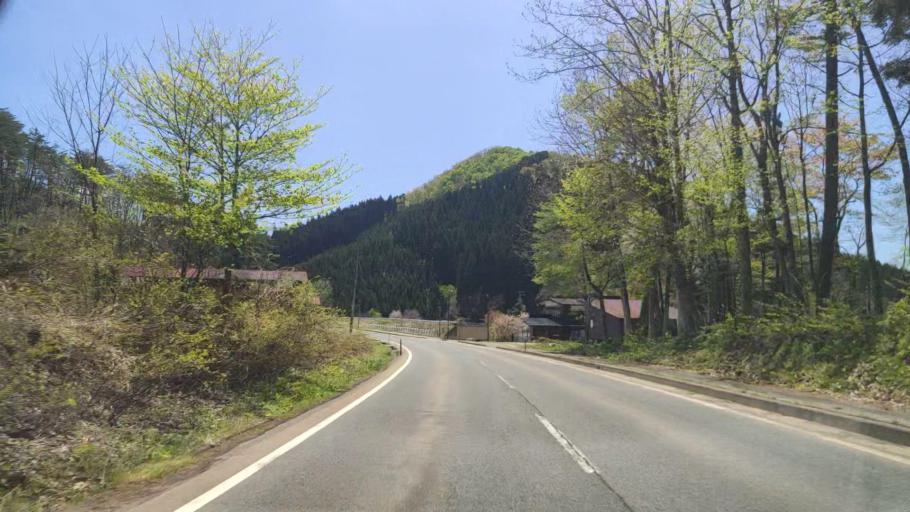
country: JP
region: Yamagata
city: Shinjo
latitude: 38.9102
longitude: 140.3232
